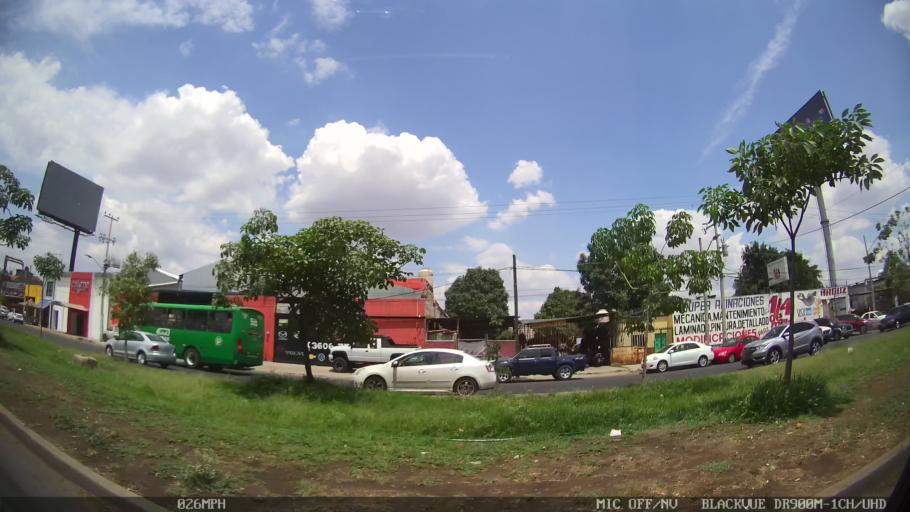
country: MX
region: Jalisco
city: Tlaquepaque
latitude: 20.6424
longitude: -103.2815
